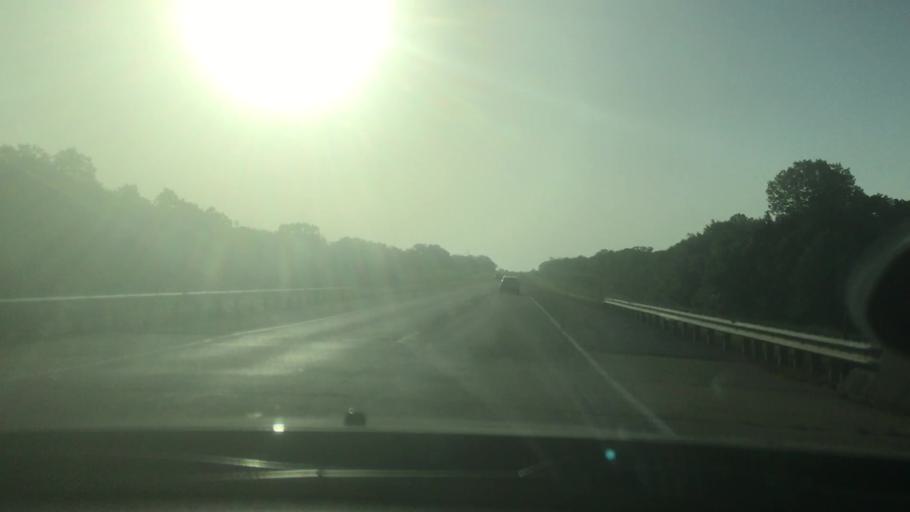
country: US
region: Oklahoma
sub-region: Pontotoc County
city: Ada
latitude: 34.6423
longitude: -96.5153
